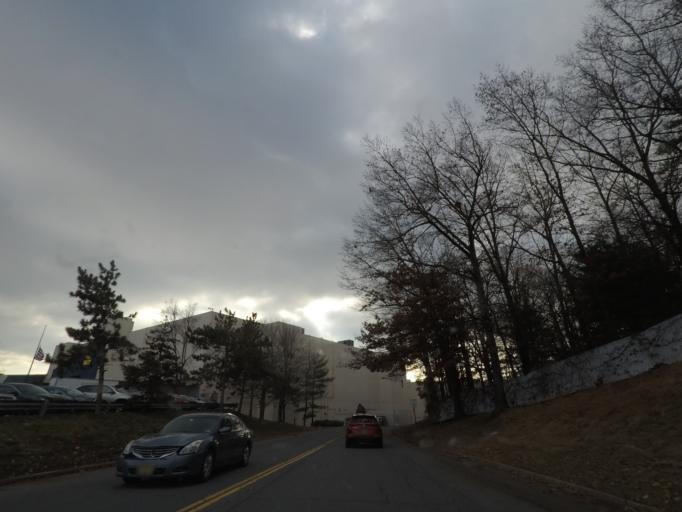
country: US
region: New York
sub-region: Albany County
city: McKownville
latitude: 42.6909
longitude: -73.8498
